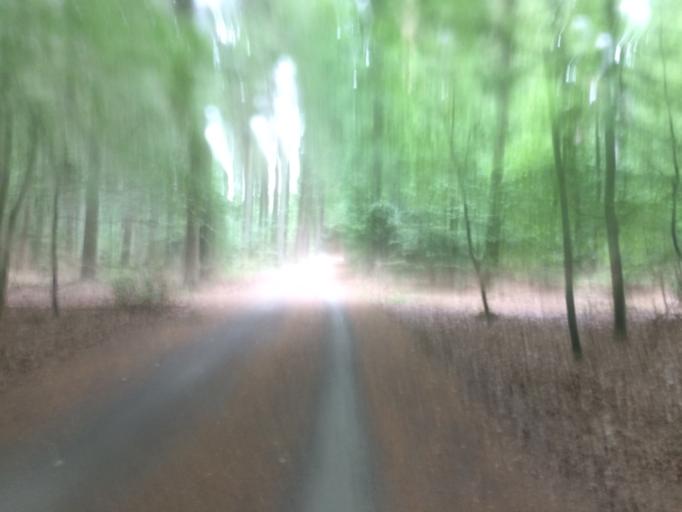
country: DK
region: Capital Region
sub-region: Bornholm Kommune
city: Ronne
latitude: 55.1360
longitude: 14.7165
